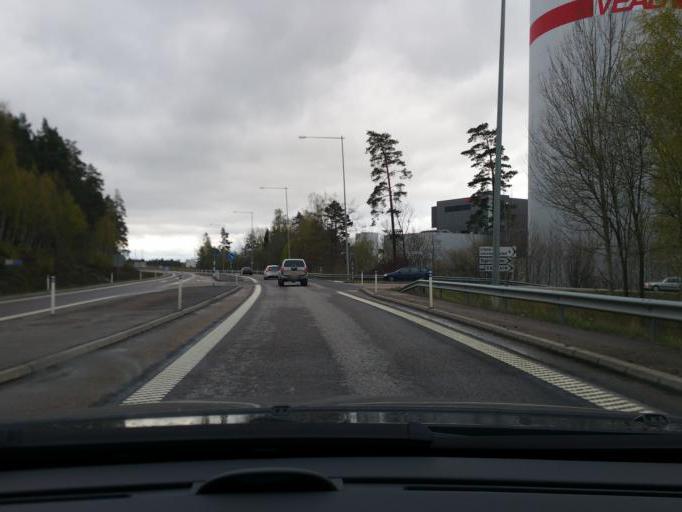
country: SE
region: Kronoberg
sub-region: Vaxjo Kommun
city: Vaexjoe
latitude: 56.8698
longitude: 14.8386
